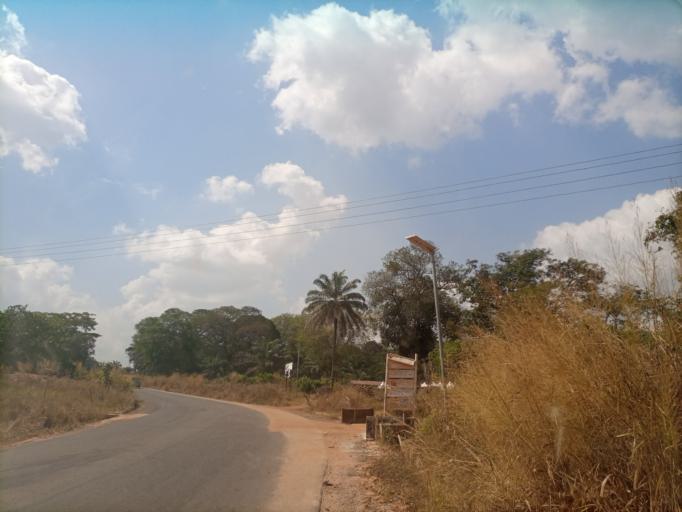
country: NG
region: Enugu
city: Obollo-Afor
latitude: 6.8815
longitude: 7.5185
